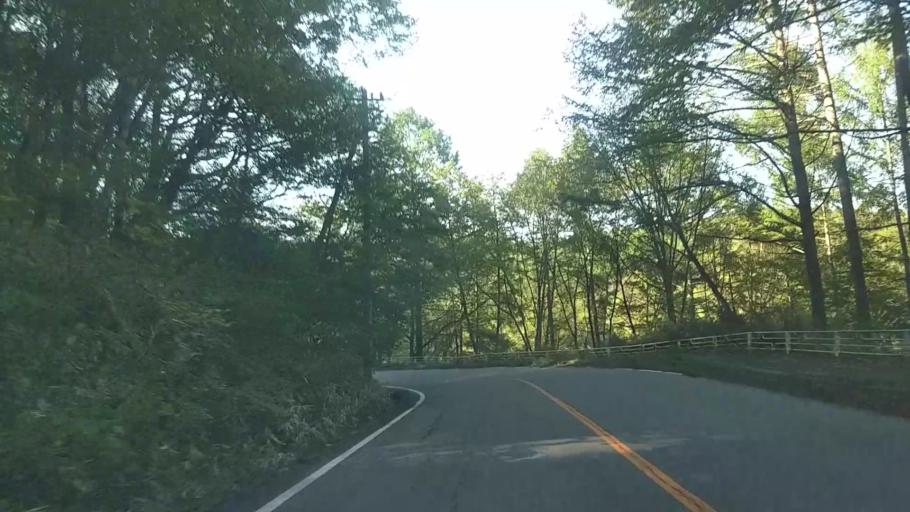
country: JP
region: Yamanashi
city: Nirasaki
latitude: 35.9041
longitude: 138.3854
